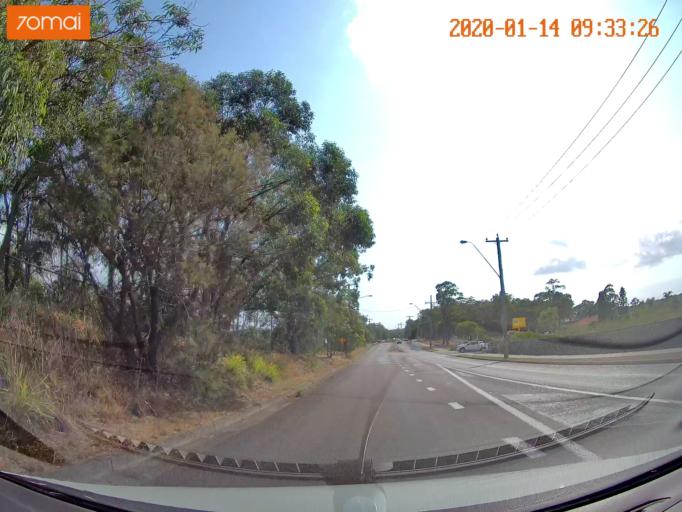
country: AU
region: New South Wales
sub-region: Lake Macquarie Shire
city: Dora Creek
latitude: -33.1101
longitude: 151.5321
